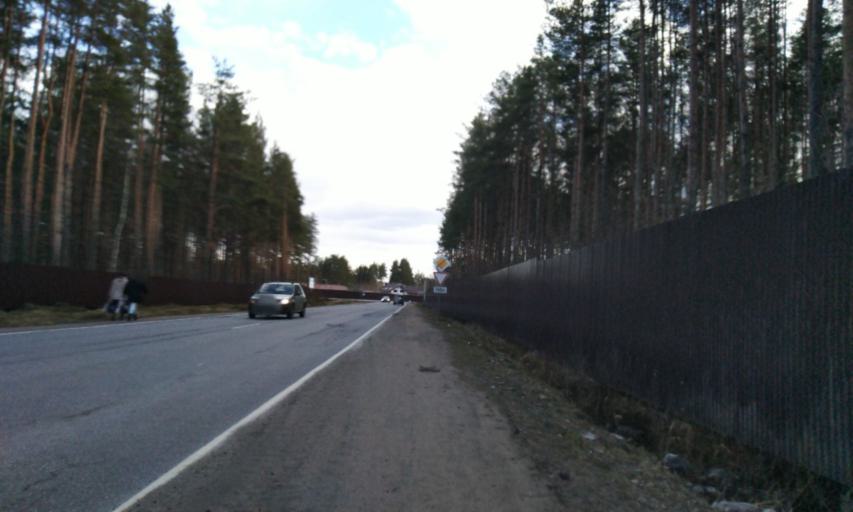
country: RU
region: Leningrad
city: Novoye Devyatkino
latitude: 60.1153
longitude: 30.4502
